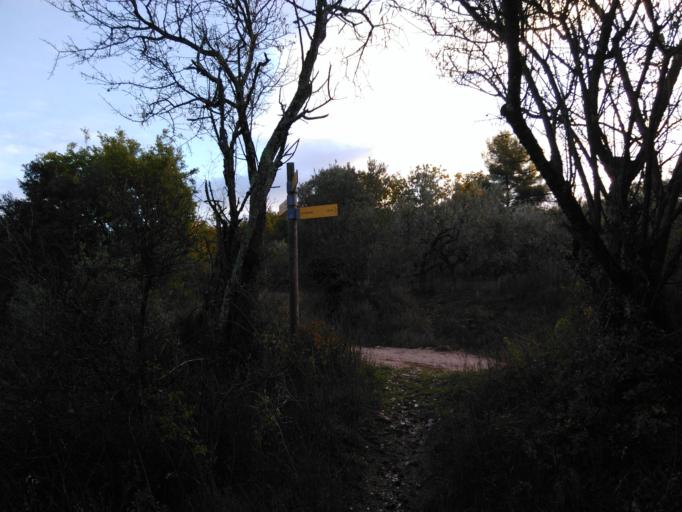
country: FR
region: Provence-Alpes-Cote d'Azur
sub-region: Departement du Vaucluse
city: Mormoiron
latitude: 44.0667
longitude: 5.1645
